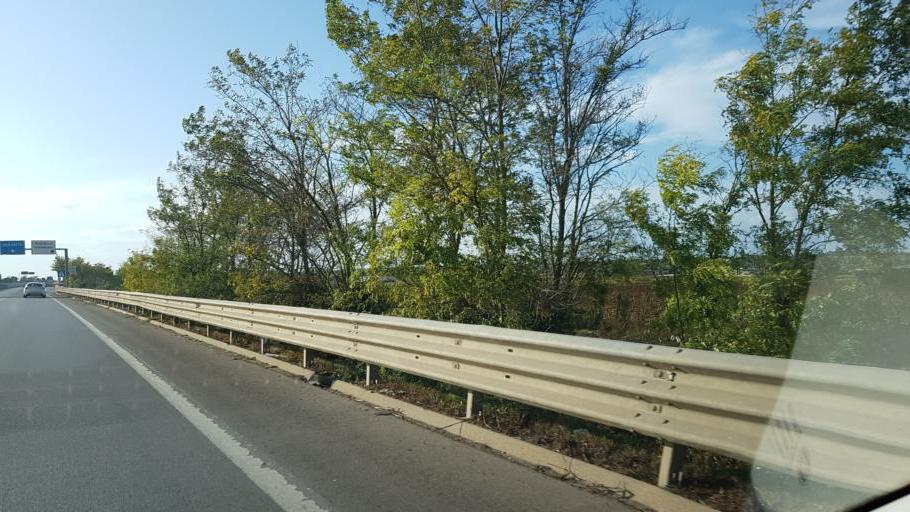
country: IT
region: Apulia
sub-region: Provincia di Brindisi
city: Francavilla Fontana
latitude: 40.5466
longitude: 17.5793
